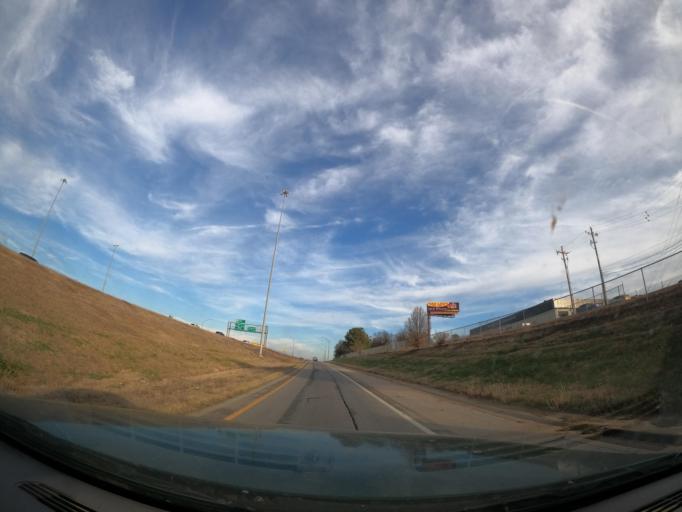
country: US
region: Oklahoma
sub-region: Tulsa County
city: Bixby
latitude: 36.0250
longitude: -95.8842
